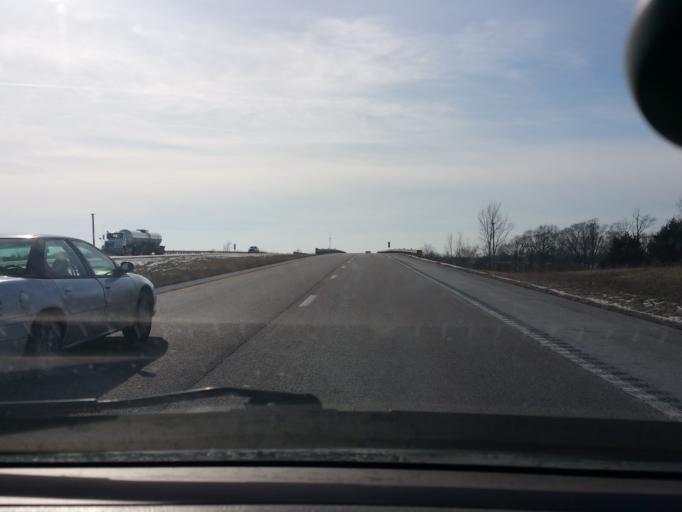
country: US
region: Missouri
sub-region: Clinton County
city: Lathrop
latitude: 39.5153
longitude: -94.2861
